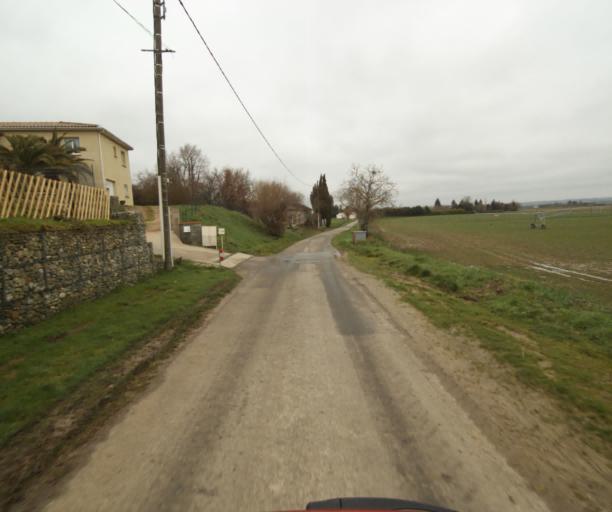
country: FR
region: Midi-Pyrenees
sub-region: Departement de l'Ariege
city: Saverdun
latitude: 43.2567
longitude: 1.5308
